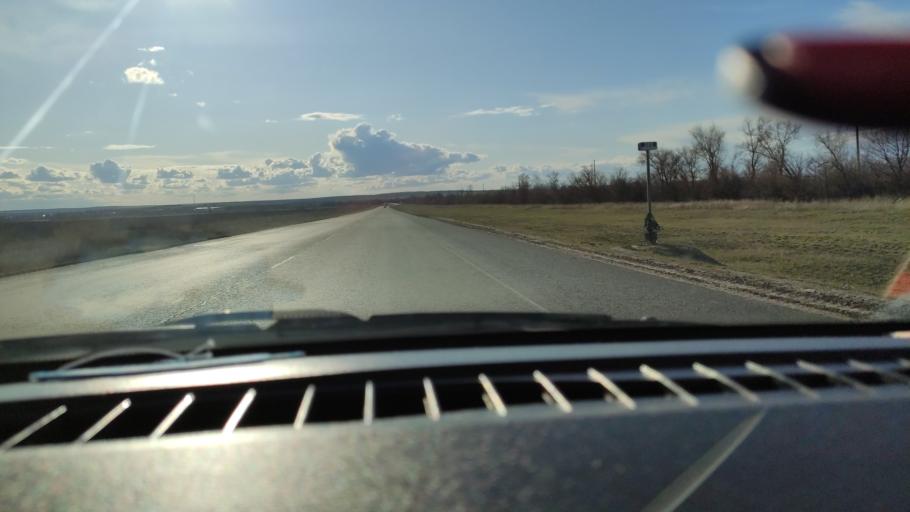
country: RU
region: Saratov
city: Yelshanka
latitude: 51.8292
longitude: 46.2505
